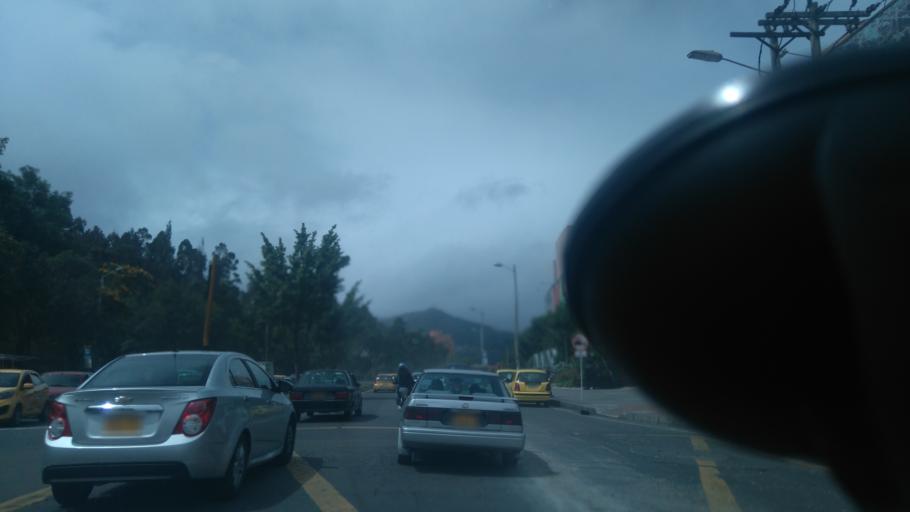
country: CO
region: Bogota D.C.
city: Barrio San Luis
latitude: 4.7163
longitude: -74.0289
